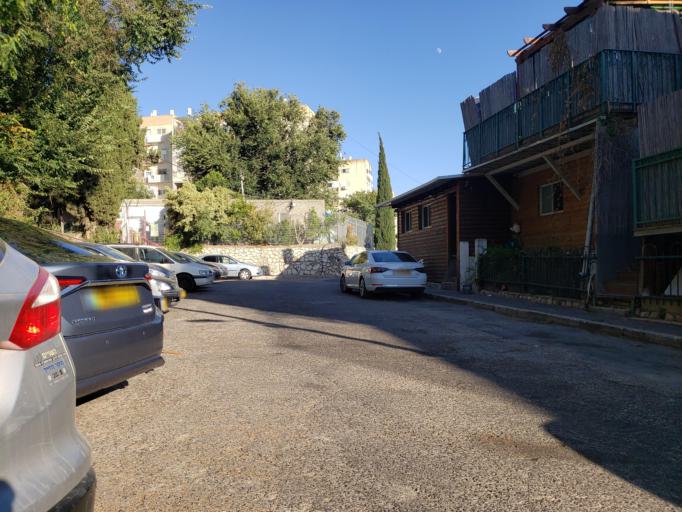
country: IL
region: Northern District
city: Safed
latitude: 32.9592
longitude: 35.4929
